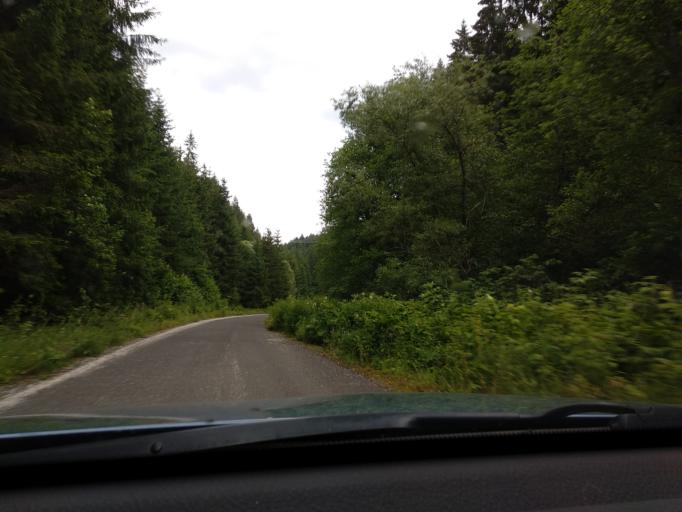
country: SK
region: Zilinsky
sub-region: Okres Liptovsky Mikulas
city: Hybe
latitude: 49.0151
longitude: 19.8600
